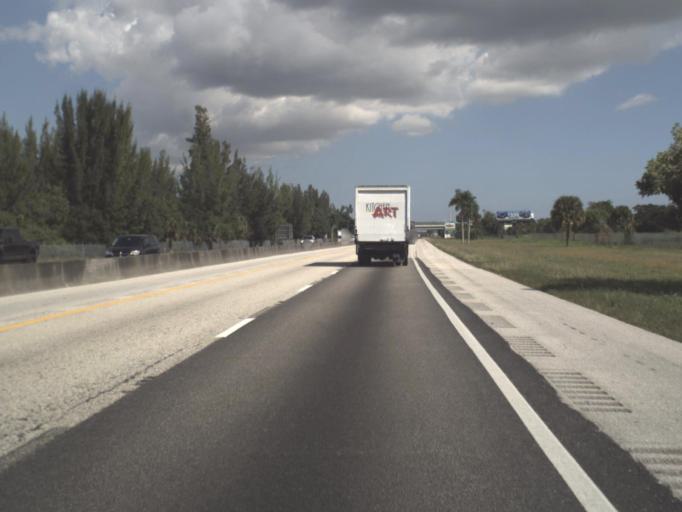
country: US
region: Florida
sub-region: Palm Beach County
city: Lake Belvedere Estates
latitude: 26.6883
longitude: -80.1598
